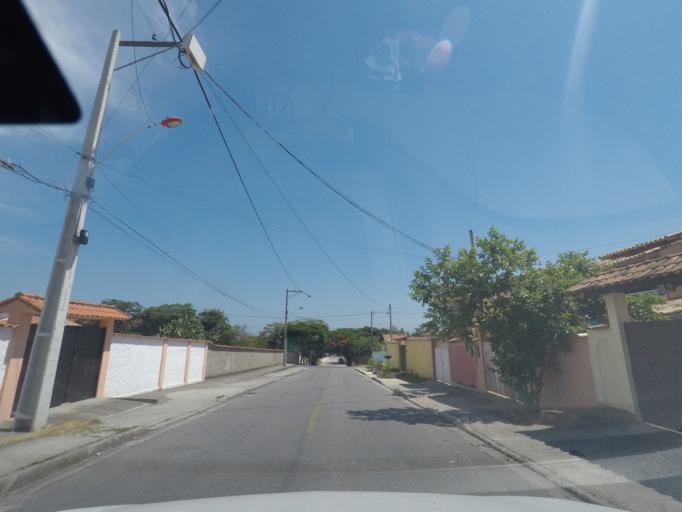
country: BR
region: Rio de Janeiro
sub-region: Marica
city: Marica
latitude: -22.9666
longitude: -42.9594
